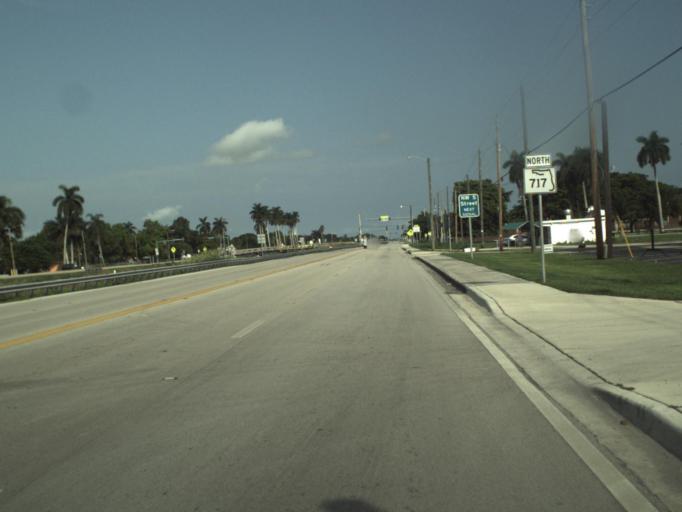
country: US
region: Florida
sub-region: Palm Beach County
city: Belle Glade
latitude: 26.6875
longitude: -80.6700
